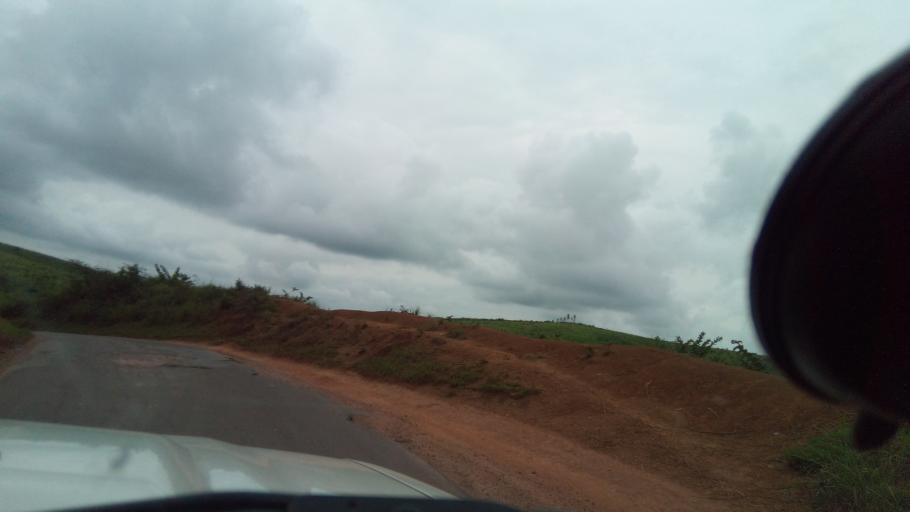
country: CD
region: Bas-Congo
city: Kasangulu
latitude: -4.9342
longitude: 15.1442
